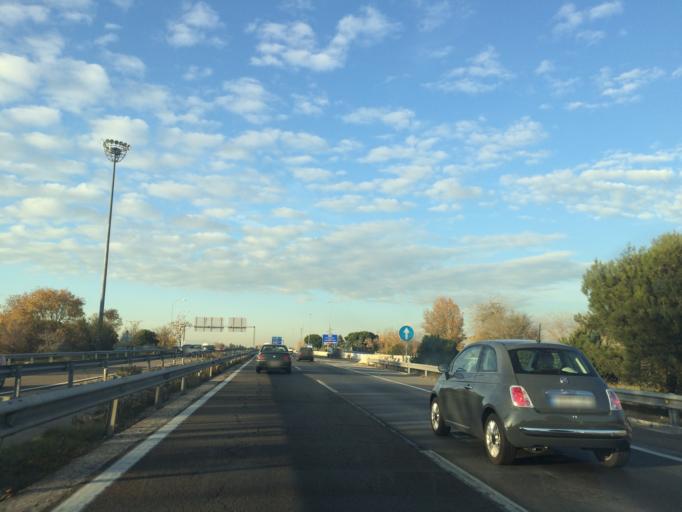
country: ES
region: Madrid
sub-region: Provincia de Madrid
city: Las Tablas
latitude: 40.5211
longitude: -3.6873
